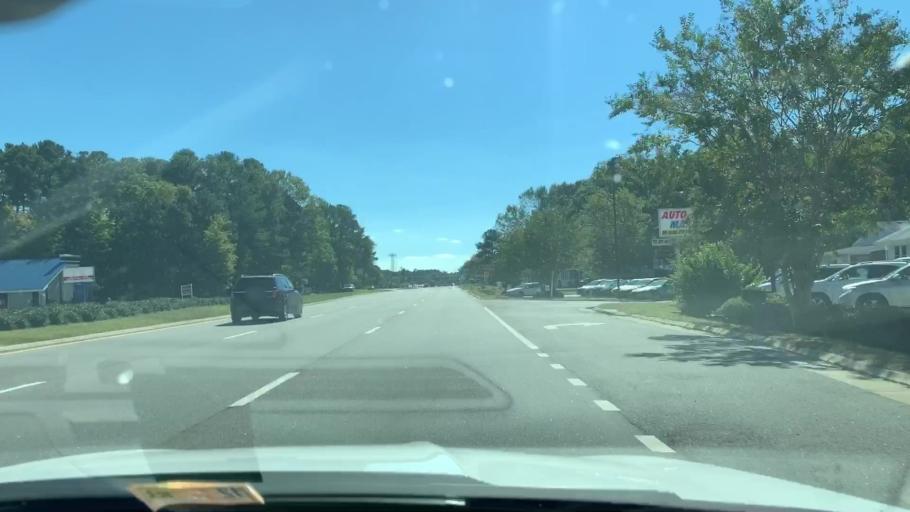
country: US
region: Virginia
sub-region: York County
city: Yorktown
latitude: 37.1516
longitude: -76.4606
